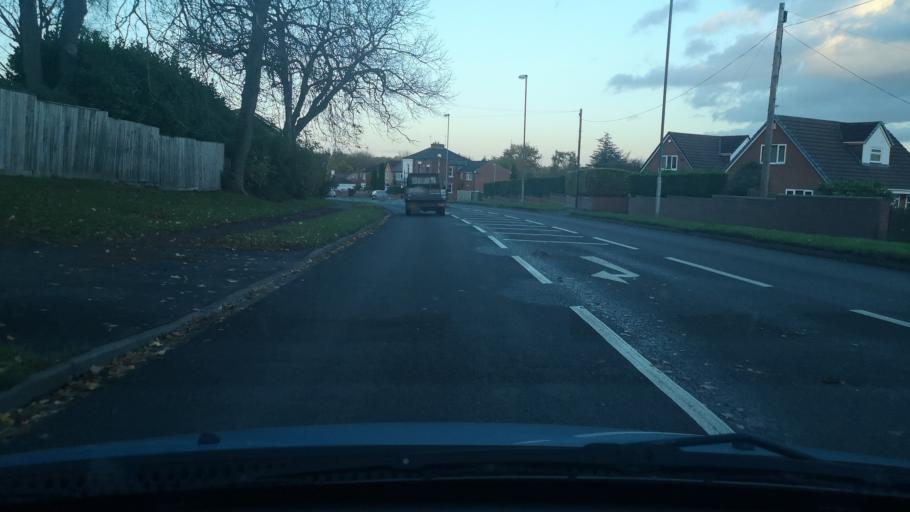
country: GB
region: England
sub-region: City and Borough of Wakefield
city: Horbury
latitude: 53.6632
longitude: -1.5423
